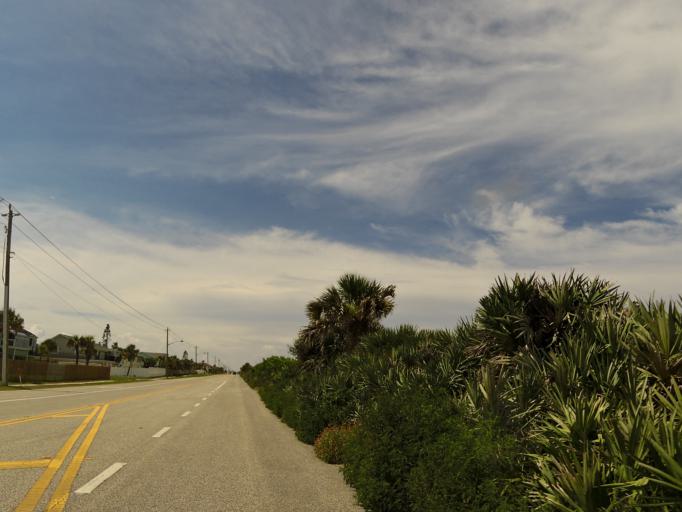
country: US
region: Florida
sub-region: Volusia County
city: Ormond-by-the-Sea
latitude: 29.3805
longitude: -81.0813
